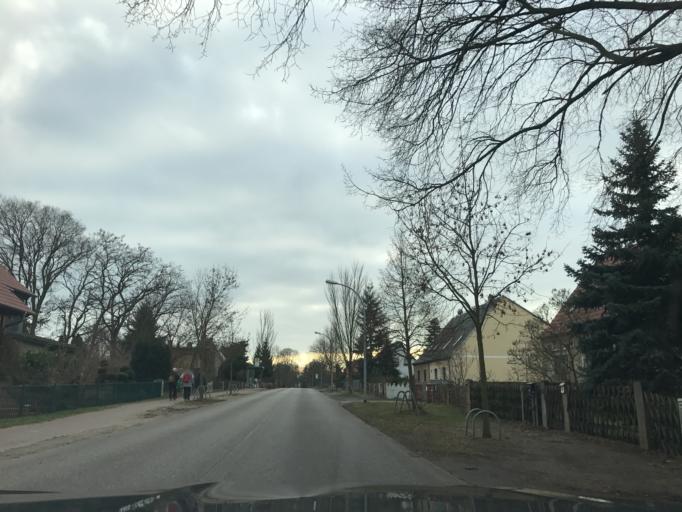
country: DE
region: Brandenburg
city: Brandenburg an der Havel
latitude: 52.3858
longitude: 12.5451
